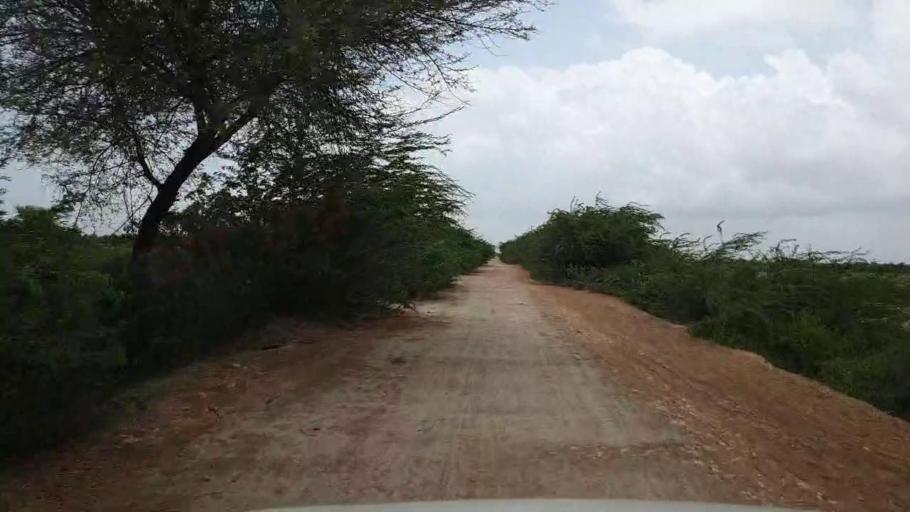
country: PK
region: Sindh
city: Kario
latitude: 24.6912
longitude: 68.6619
